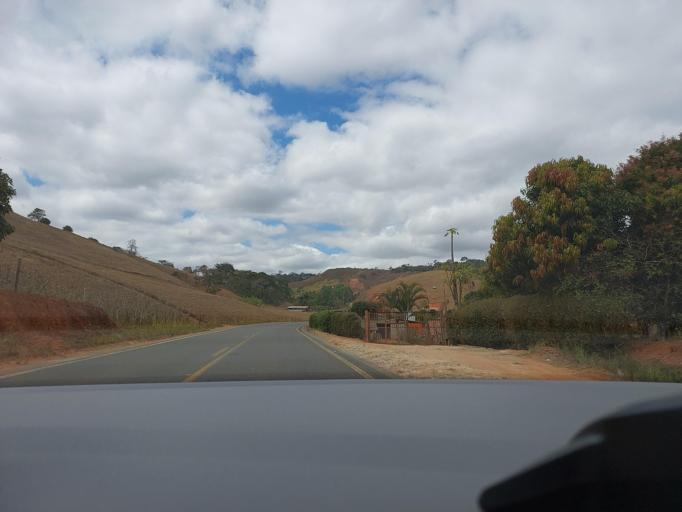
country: BR
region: Minas Gerais
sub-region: Vicosa
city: Vicosa
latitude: -20.8320
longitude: -42.7252
